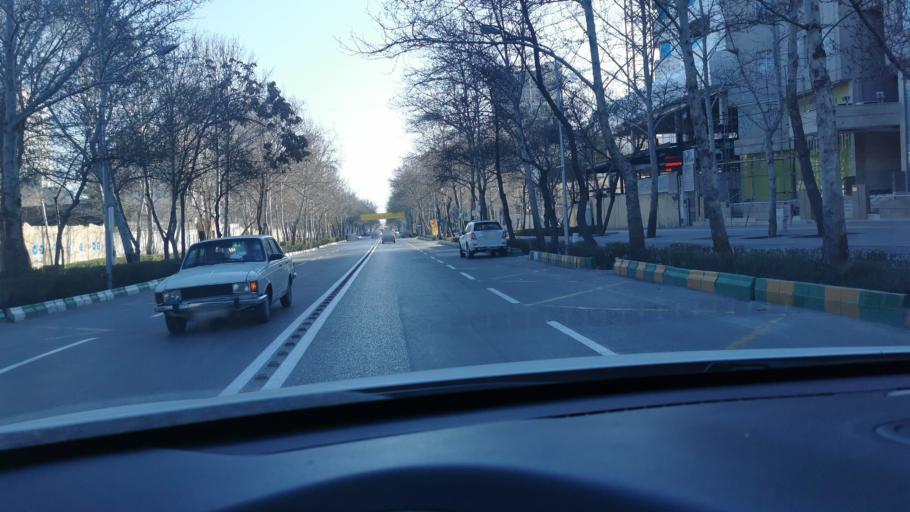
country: IR
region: Razavi Khorasan
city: Mashhad
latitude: 36.2848
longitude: 59.5680
